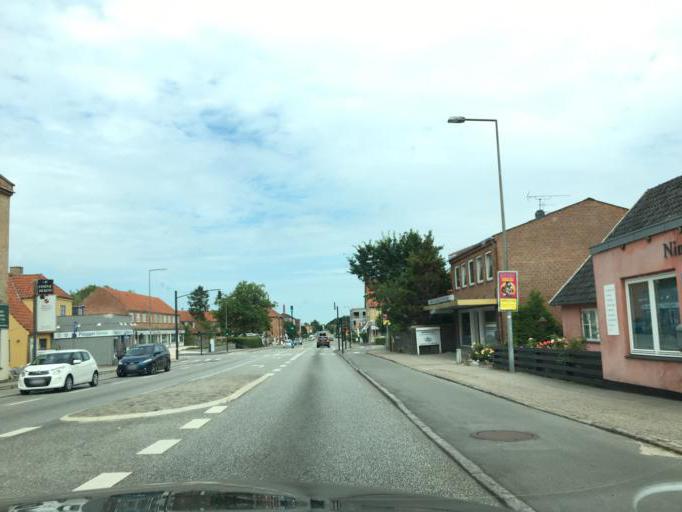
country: DK
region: Capital Region
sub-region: Horsholm Kommune
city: Horsholm
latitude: 55.8842
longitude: 12.4980
